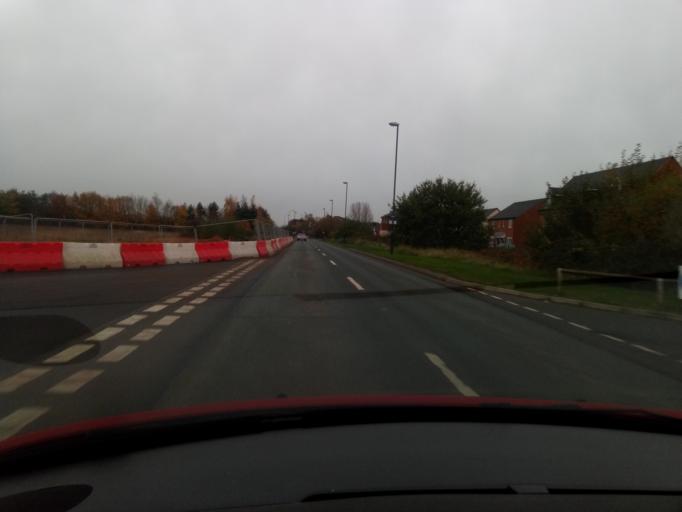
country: GB
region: England
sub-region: Derbyshire
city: Borrowash
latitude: 52.8801
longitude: -1.4103
